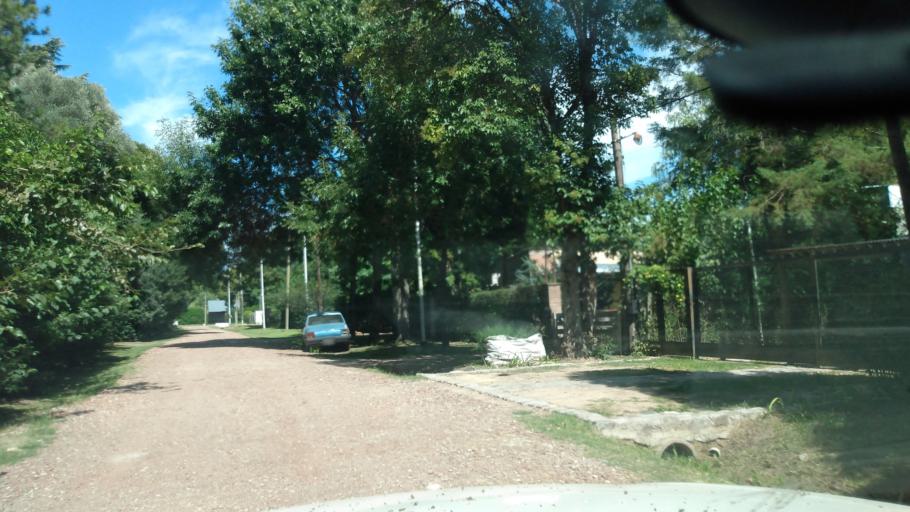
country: AR
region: Buenos Aires
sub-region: Partido de Lujan
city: Lujan
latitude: -34.5502
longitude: -59.1490
